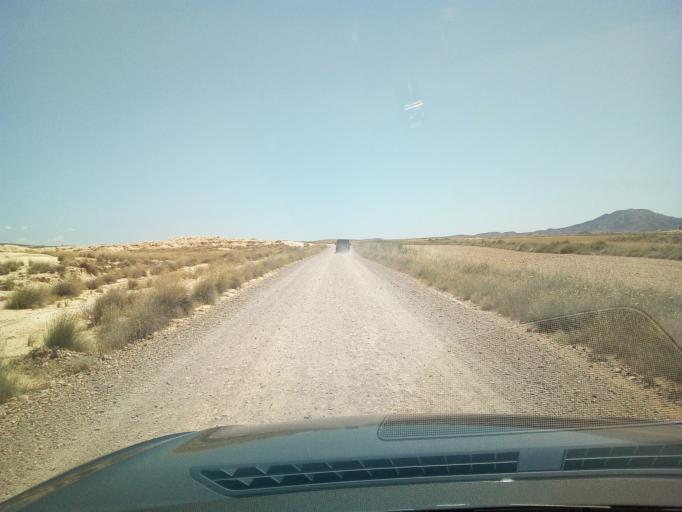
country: ES
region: Navarre
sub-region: Provincia de Navarra
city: Arguedas
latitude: 42.1817
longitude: -1.4658
